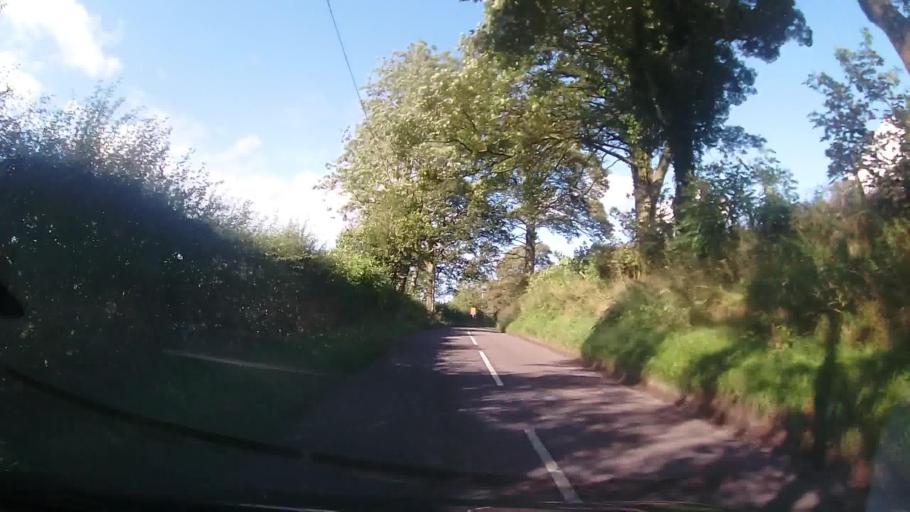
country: GB
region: England
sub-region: Shropshire
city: Norbury
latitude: 52.5716
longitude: -2.8901
